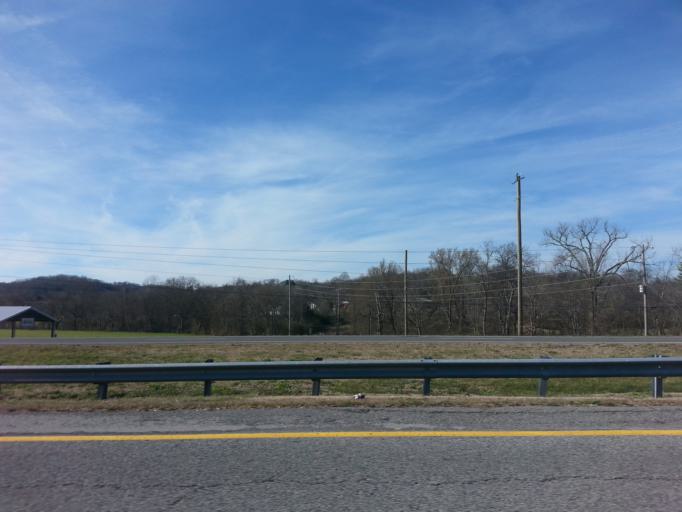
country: US
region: Tennessee
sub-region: Cannon County
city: Woodbury
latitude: 35.8228
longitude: -86.0908
